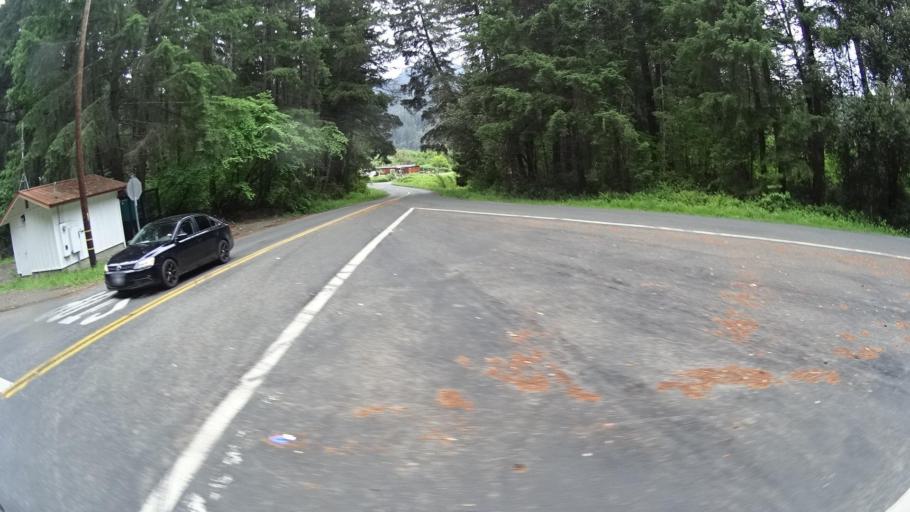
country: US
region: California
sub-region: Humboldt County
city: Willow Creek
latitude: 41.0498
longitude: -123.6660
